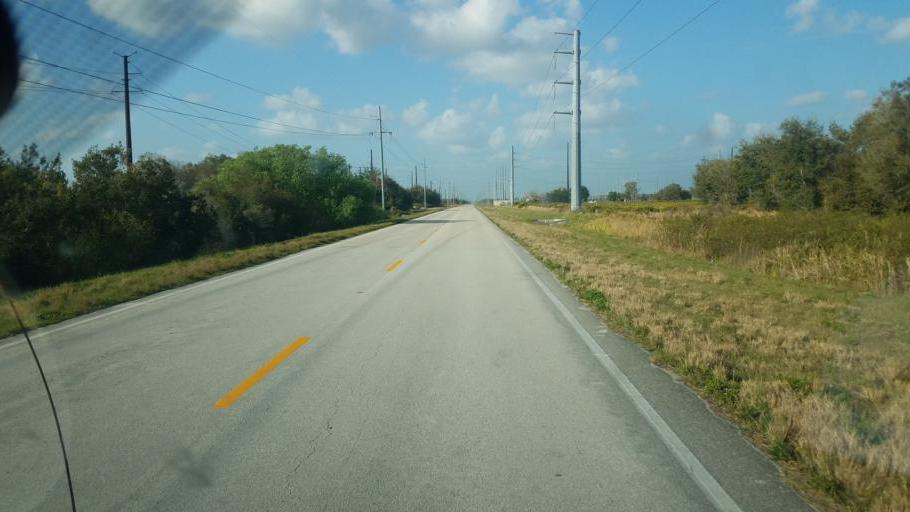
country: US
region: Florida
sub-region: Hardee County
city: Wauchula
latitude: 27.5188
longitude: -81.9259
